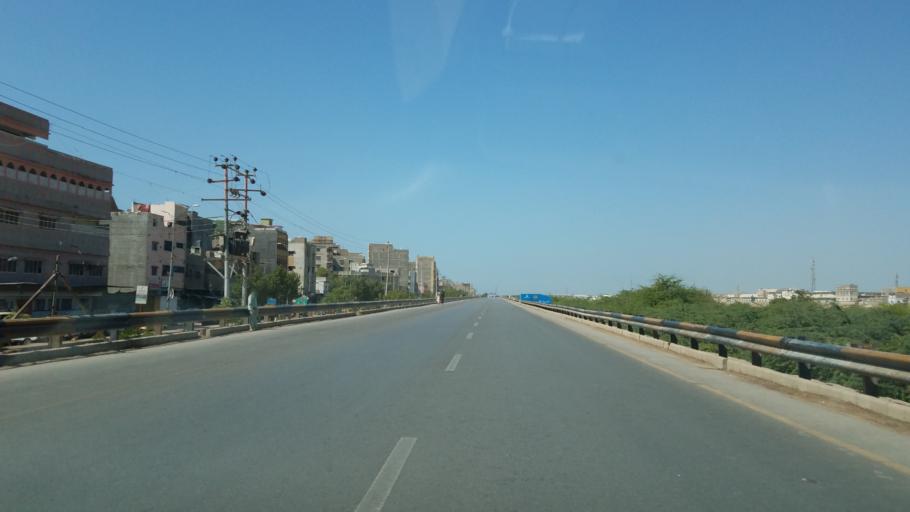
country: PK
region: Sindh
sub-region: Karachi District
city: Karachi
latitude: 24.8776
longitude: 66.9902
